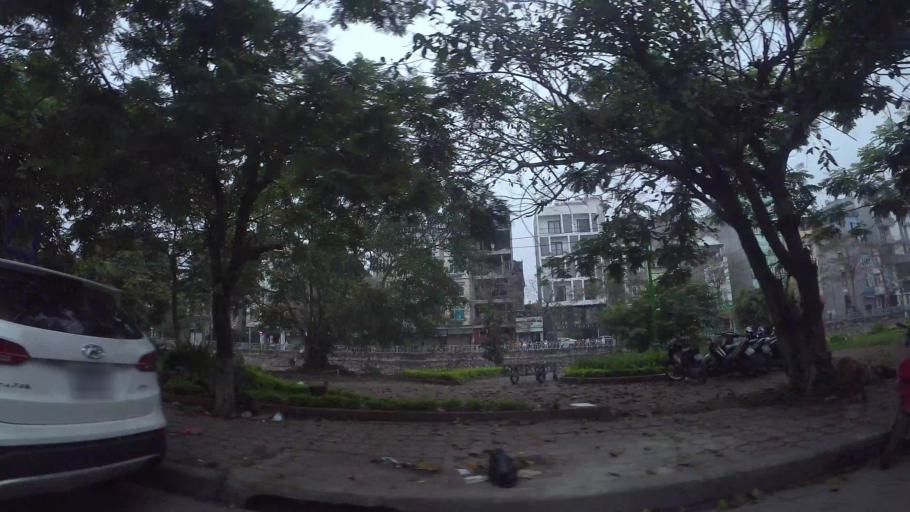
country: VN
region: Ha Noi
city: Hai BaTrung
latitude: 20.9888
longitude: 105.8438
